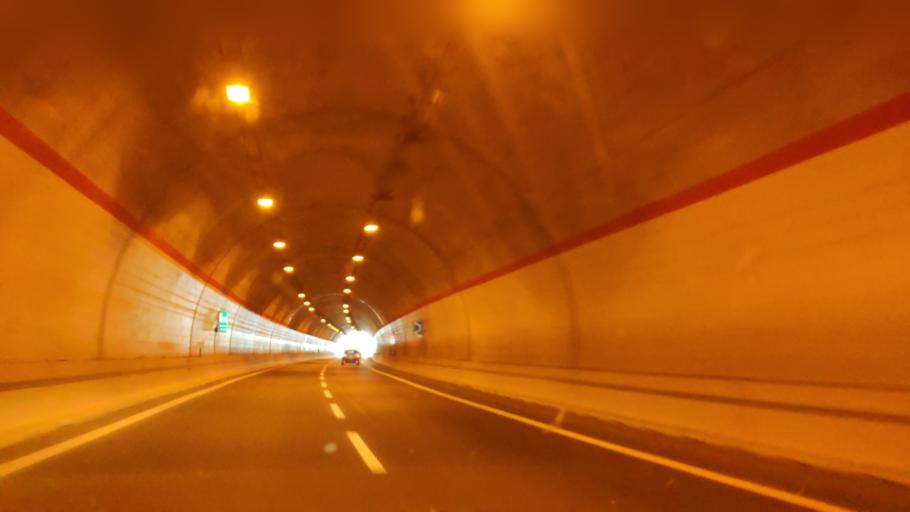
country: IT
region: Calabria
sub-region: Provincia di Reggio Calabria
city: Marina di Gioiosa Ionica
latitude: 38.3149
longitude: 16.3173
